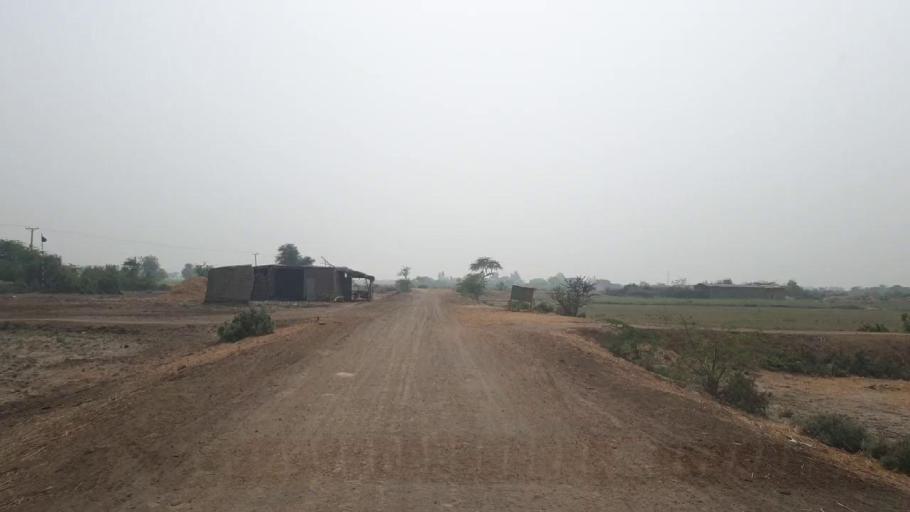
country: PK
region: Sindh
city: Kario
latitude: 24.6450
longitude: 68.6399
